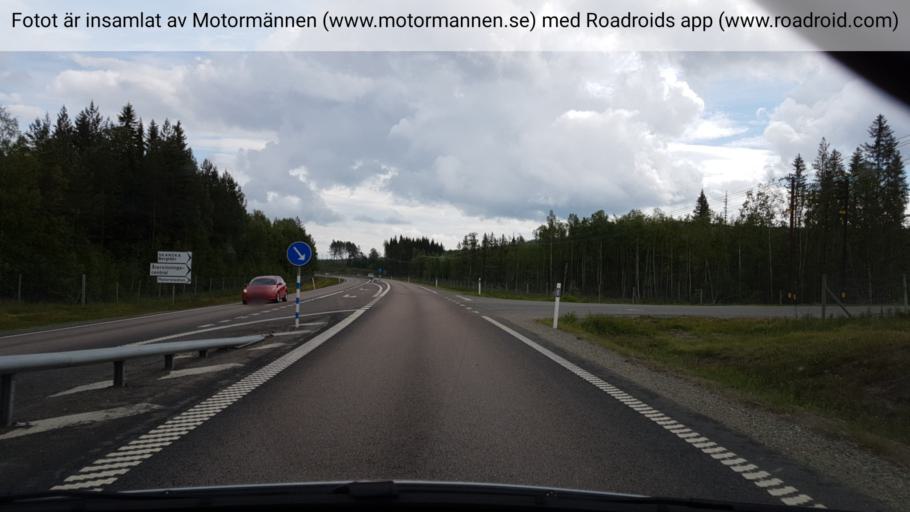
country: SE
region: Vaesternorrland
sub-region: Solleftea Kommun
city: Solleftea
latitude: 63.1619
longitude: 17.1740
